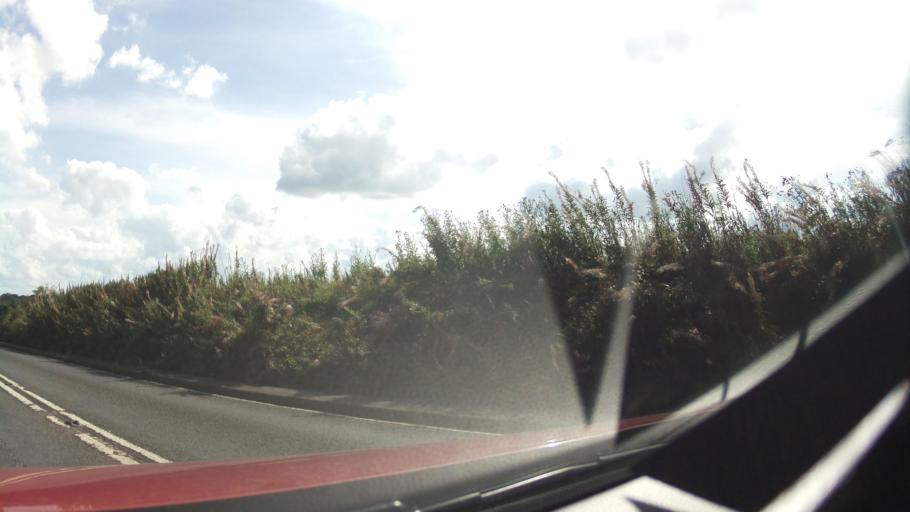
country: GB
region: Scotland
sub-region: Stirling
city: Cowie
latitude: 56.0527
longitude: -3.8605
